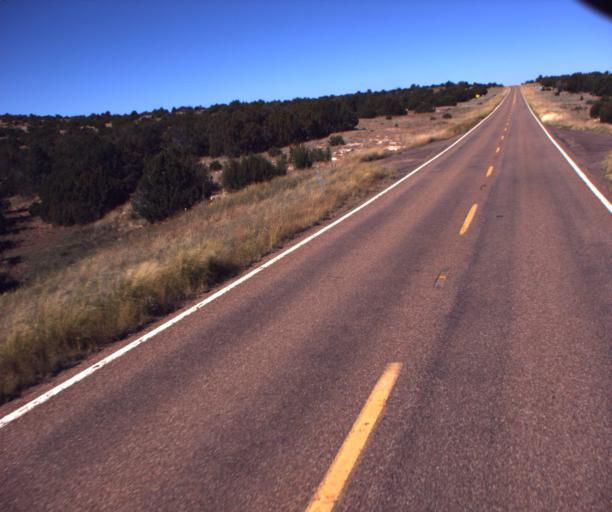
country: US
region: Arizona
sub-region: Navajo County
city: Heber-Overgaard
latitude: 34.4595
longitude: -110.4680
